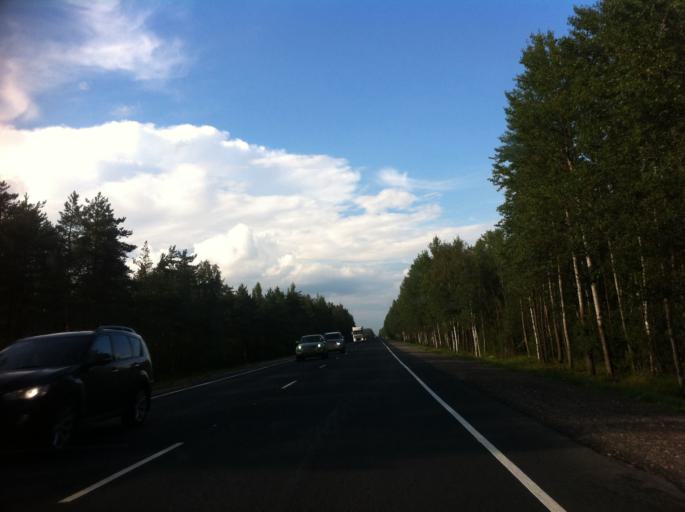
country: RU
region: Leningrad
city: Luga
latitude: 58.4439
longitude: 29.7539
